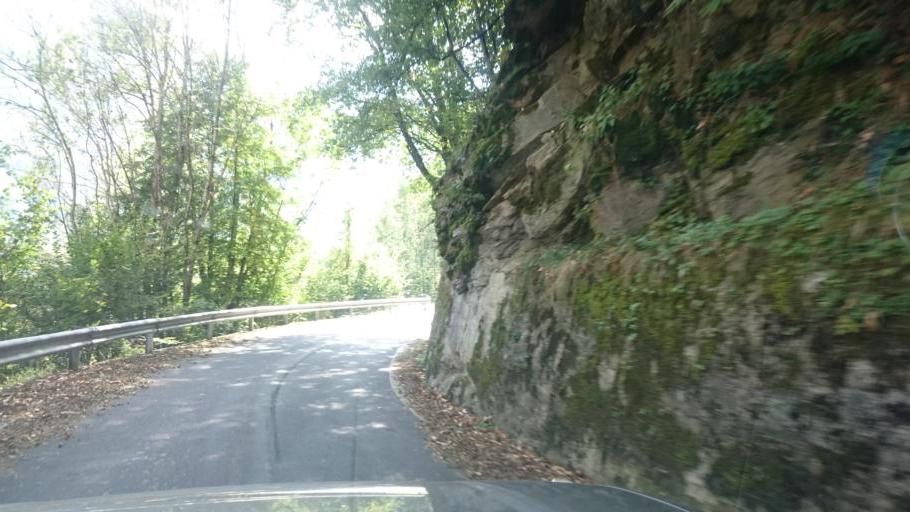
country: IT
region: Lombardy
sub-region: Provincia di Brescia
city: Paisco Loveno
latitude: 46.0717
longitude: 10.2762
